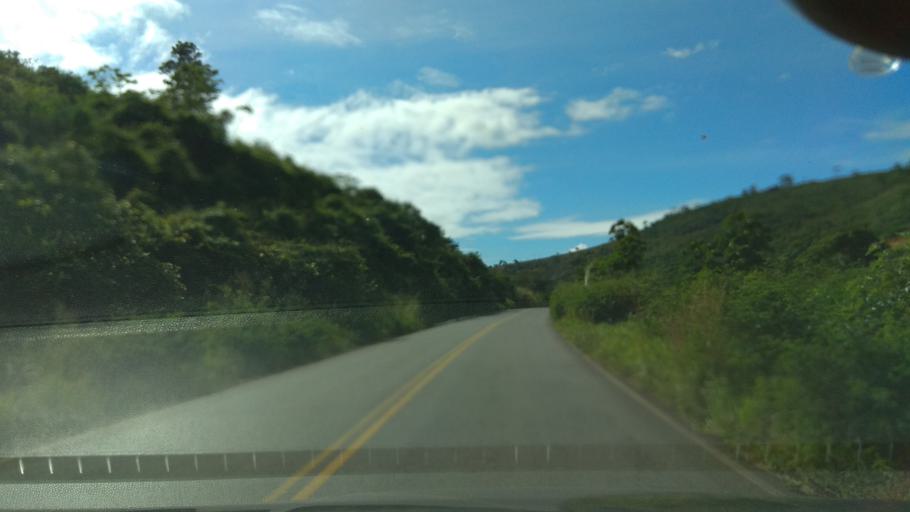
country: BR
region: Bahia
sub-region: Ubaira
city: Ubaira
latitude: -13.2633
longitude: -39.6825
